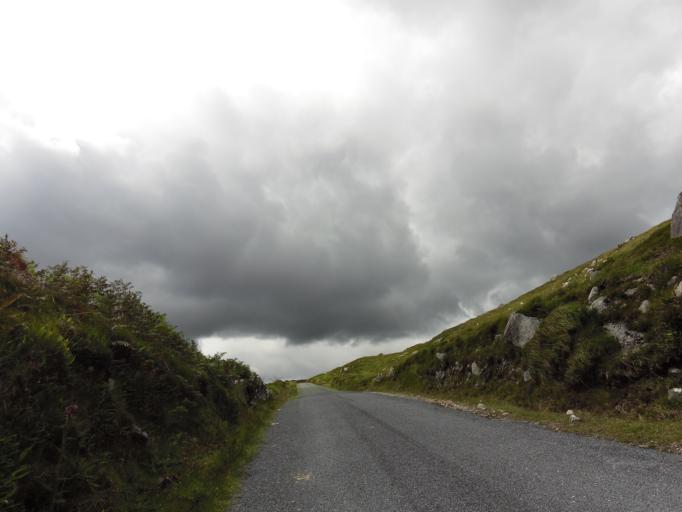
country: IE
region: Connaught
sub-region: County Galway
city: Oughterard
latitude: 53.3896
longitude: -9.3457
